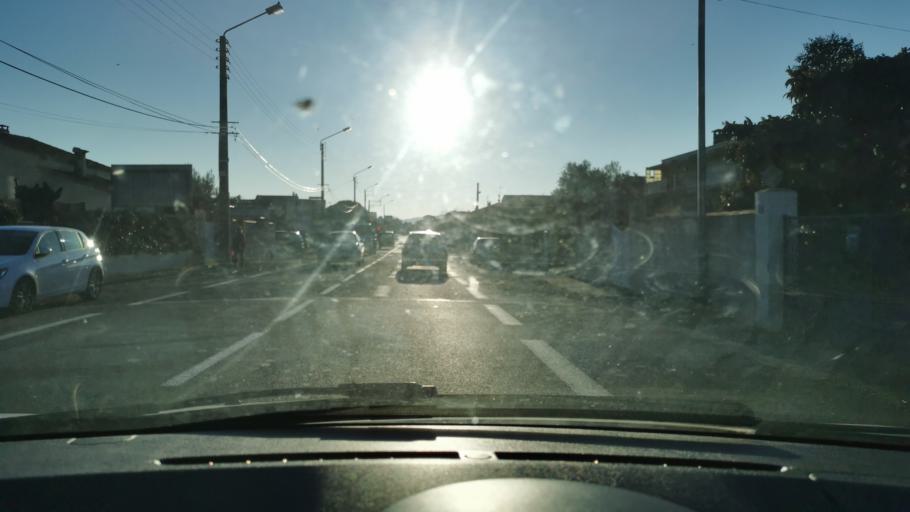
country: FR
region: Languedoc-Roussillon
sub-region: Departement de l'Herault
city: Frontignan
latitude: 43.4402
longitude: 3.7448
